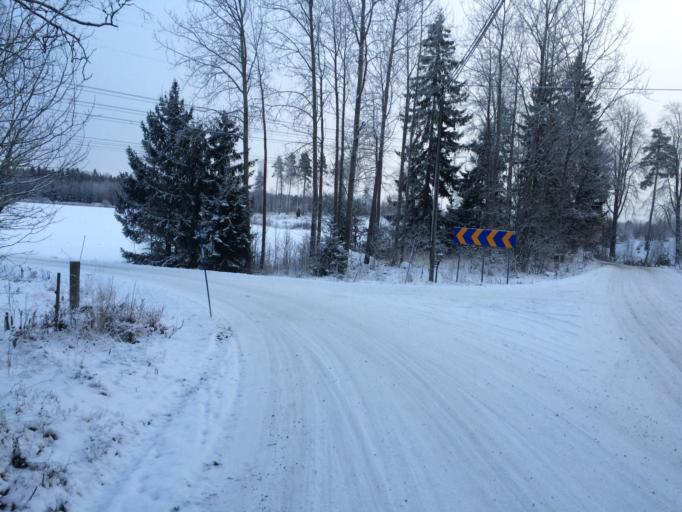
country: SE
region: Uppsala
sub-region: Enkopings Kommun
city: Orsundsbro
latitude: 59.9084
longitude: 17.1856
